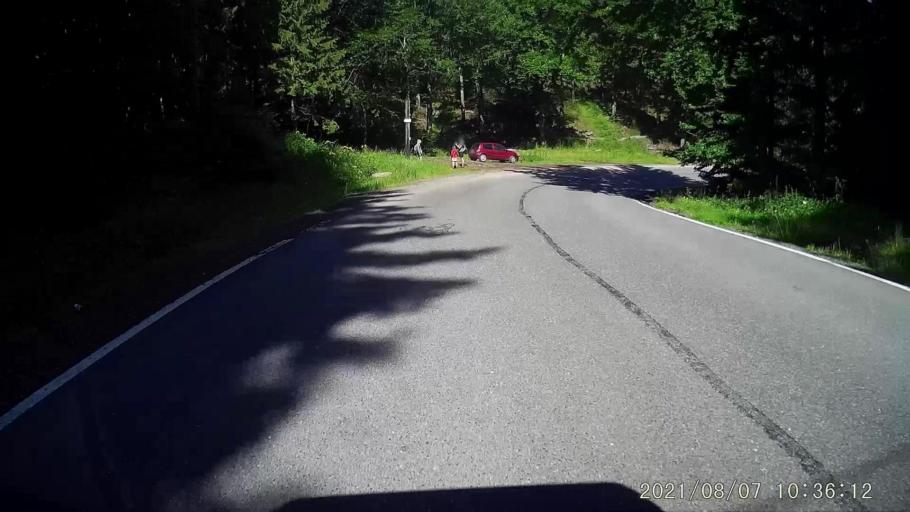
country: PL
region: Lower Silesian Voivodeship
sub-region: Powiat klodzki
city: Duszniki-Zdroj
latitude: 50.3636
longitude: 16.3692
